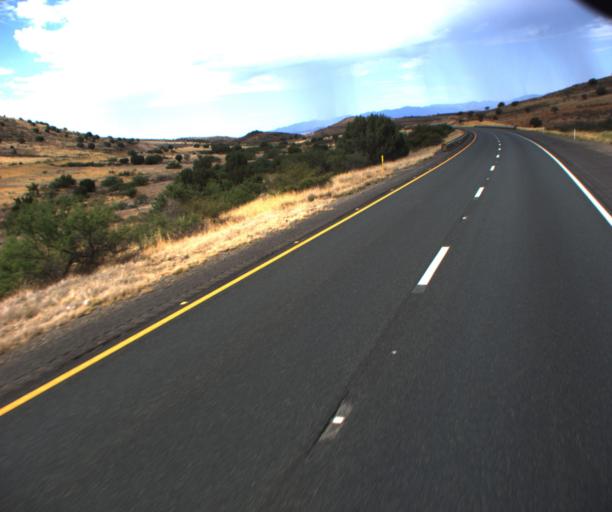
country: US
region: Arizona
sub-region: Yavapai County
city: Camp Verde
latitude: 34.4828
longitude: -112.0190
